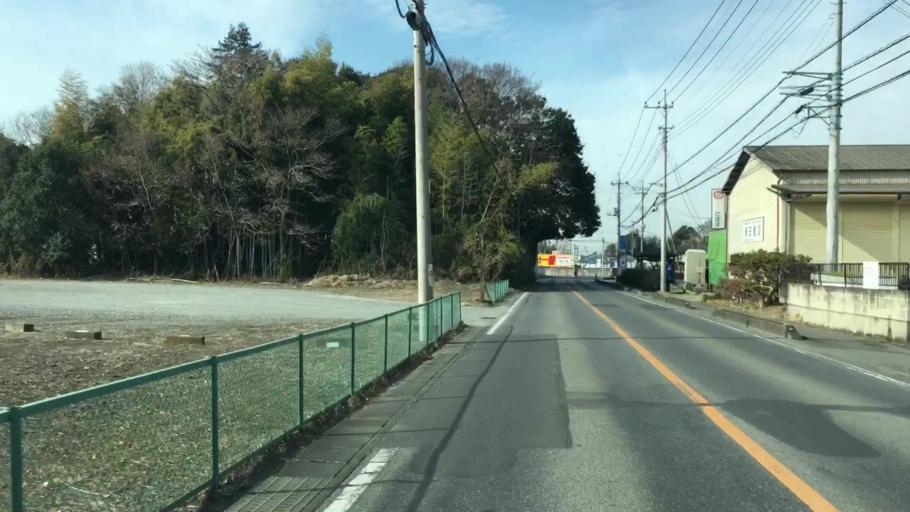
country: JP
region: Saitama
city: Menuma
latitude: 36.2474
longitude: 139.4359
